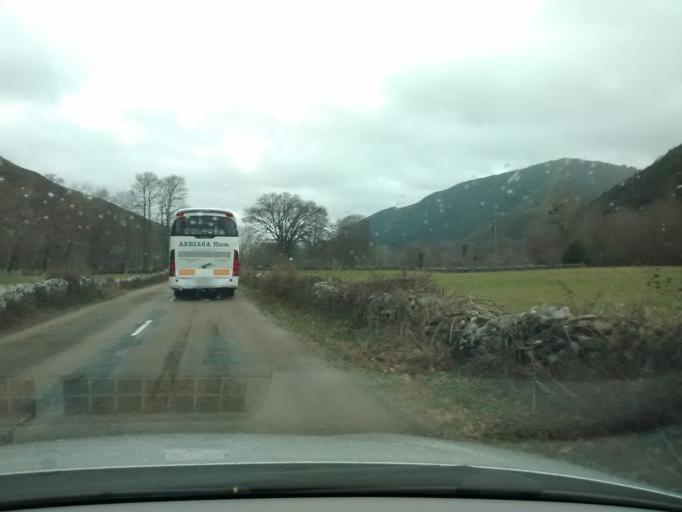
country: ES
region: Castille and Leon
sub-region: Provincia de Burgos
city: Espinosa de los Monteros
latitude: 43.1089
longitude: -3.5764
